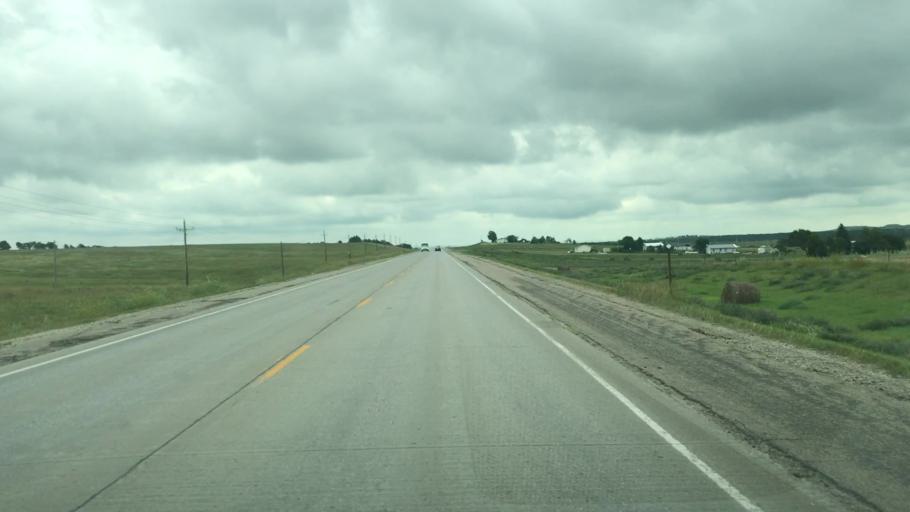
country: US
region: South Dakota
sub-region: Todd County
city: Mission
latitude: 43.3029
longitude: -100.7037
